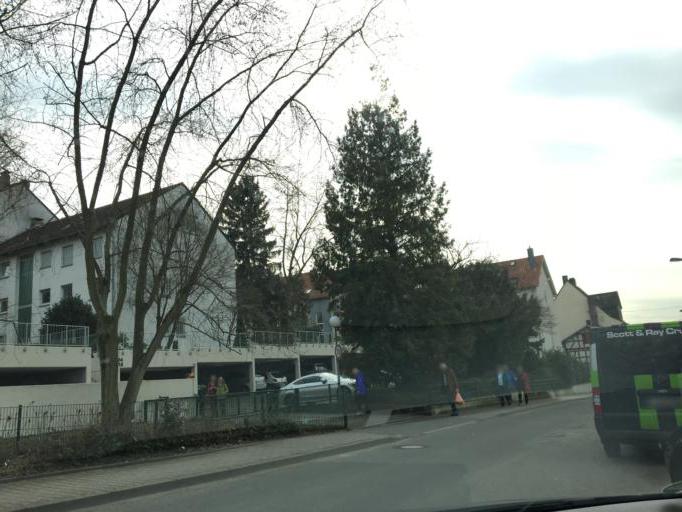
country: DE
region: Hesse
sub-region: Regierungsbezirk Darmstadt
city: Bad Vilbel
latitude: 50.1722
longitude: 8.6986
